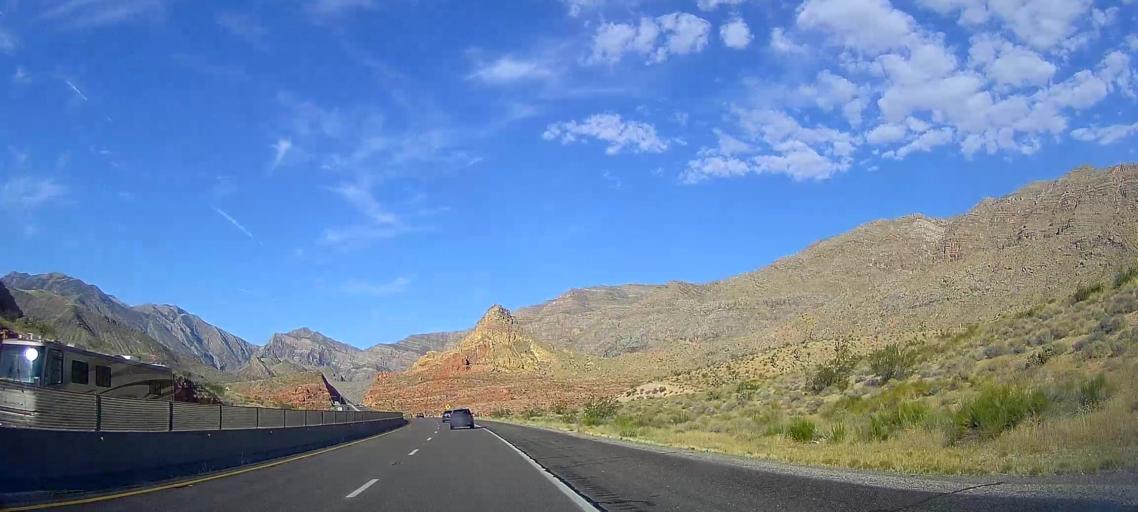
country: US
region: Arizona
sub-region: Mohave County
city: Beaver Dam
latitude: 36.9536
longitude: -113.7974
